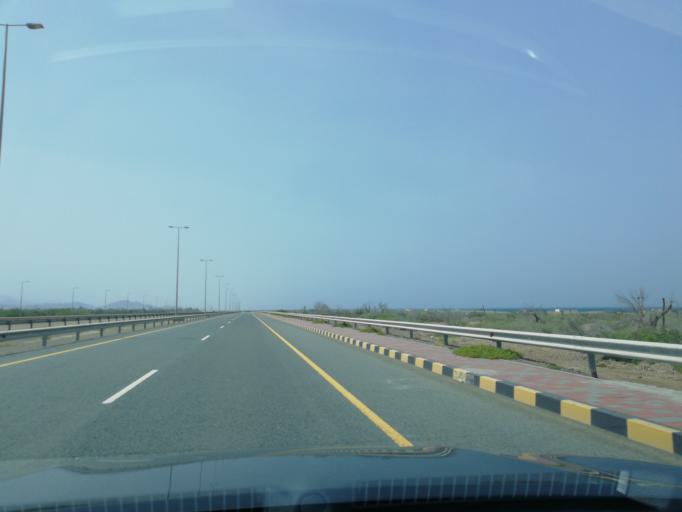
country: OM
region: Al Batinah
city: Shinas
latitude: 24.8815
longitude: 56.4039
